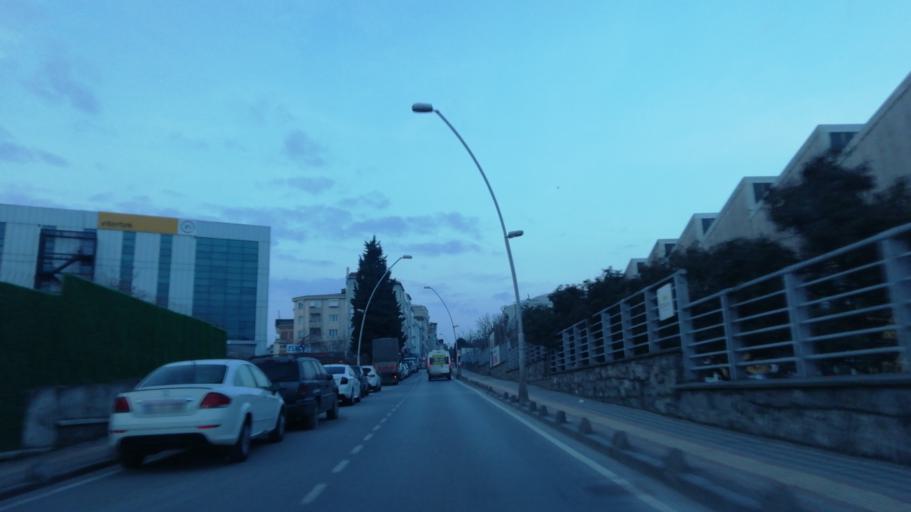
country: TR
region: Istanbul
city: Bahcelievler
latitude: 41.0058
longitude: 28.8217
